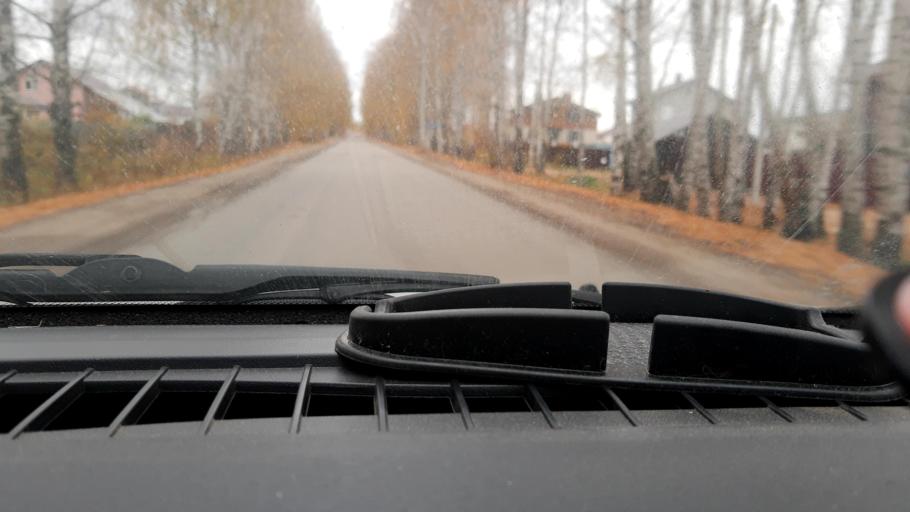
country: RU
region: Nizjnij Novgorod
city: Neklyudovo
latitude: 56.4091
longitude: 44.0244
